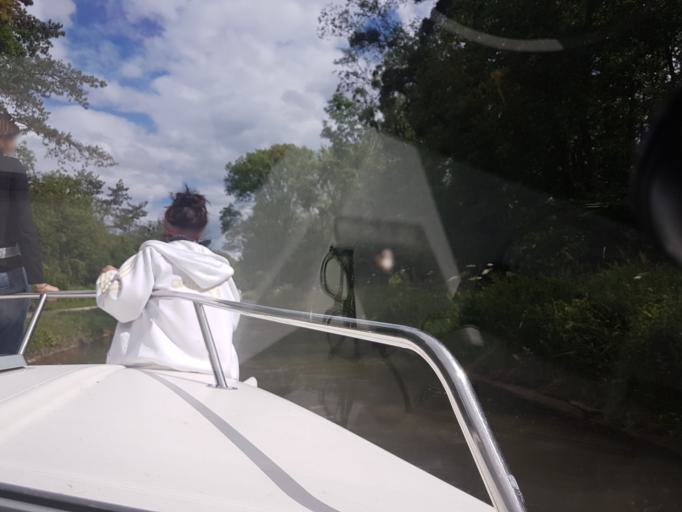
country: FR
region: Bourgogne
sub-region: Departement de l'Yonne
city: Vermenton
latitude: 47.5900
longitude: 3.6367
